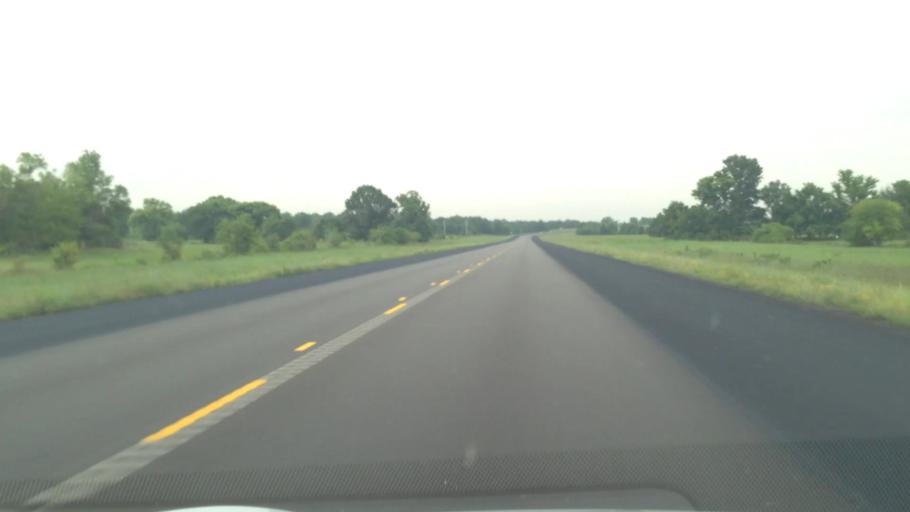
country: US
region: Kansas
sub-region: Cherokee County
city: Baxter Springs
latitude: 37.0331
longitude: -94.7057
